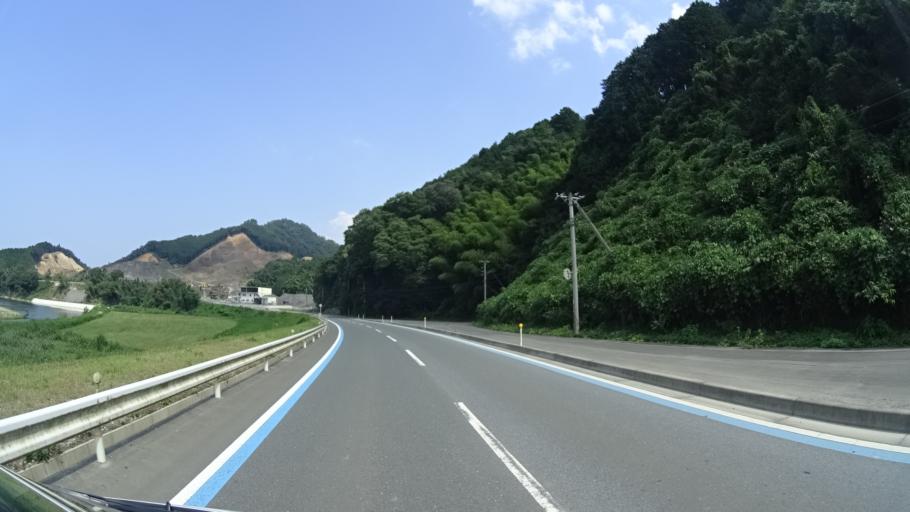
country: JP
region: Kyoto
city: Fukuchiyama
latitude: 35.3792
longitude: 135.1578
